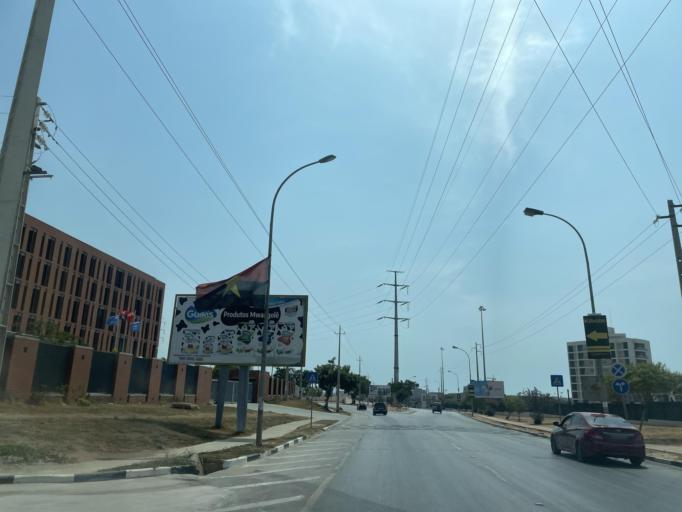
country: AO
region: Luanda
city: Luanda
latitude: -8.9142
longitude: 13.1947
